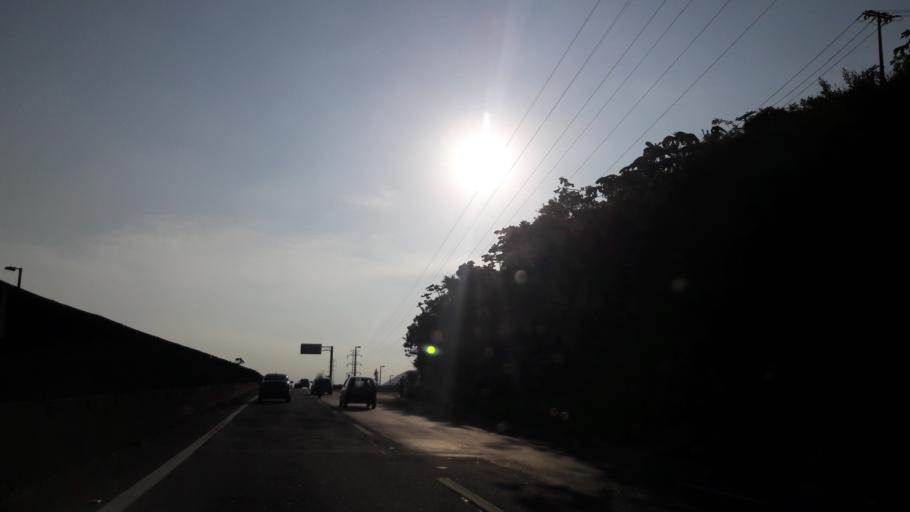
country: BR
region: Sao Paulo
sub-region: Mongagua
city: Mongagua
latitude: -24.0987
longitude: -46.6324
